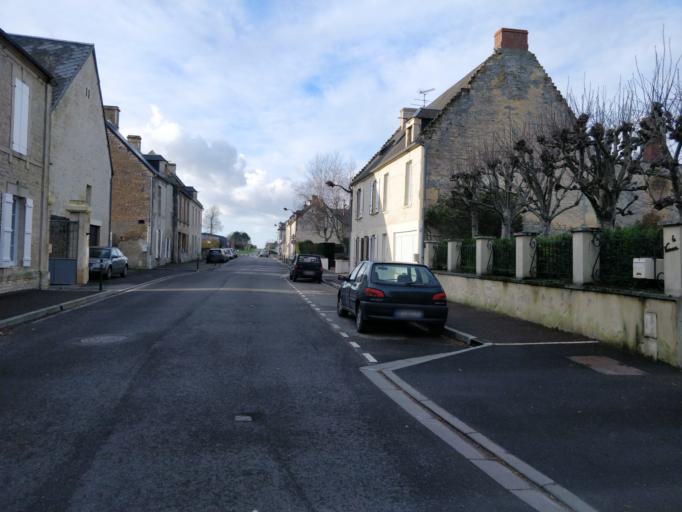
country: FR
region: Lower Normandy
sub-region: Departement du Calvados
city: Saint-Manvieu
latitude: 49.2126
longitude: -0.5192
